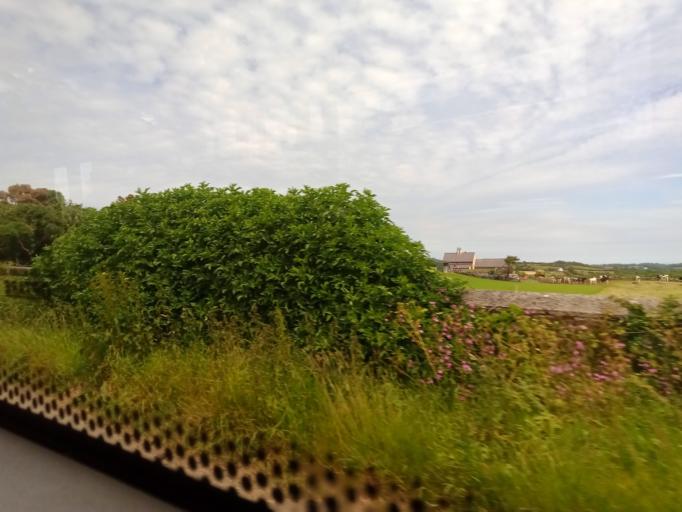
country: GB
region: Wales
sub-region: Anglesey
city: Beaumaris
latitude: 53.2805
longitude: -4.1255
